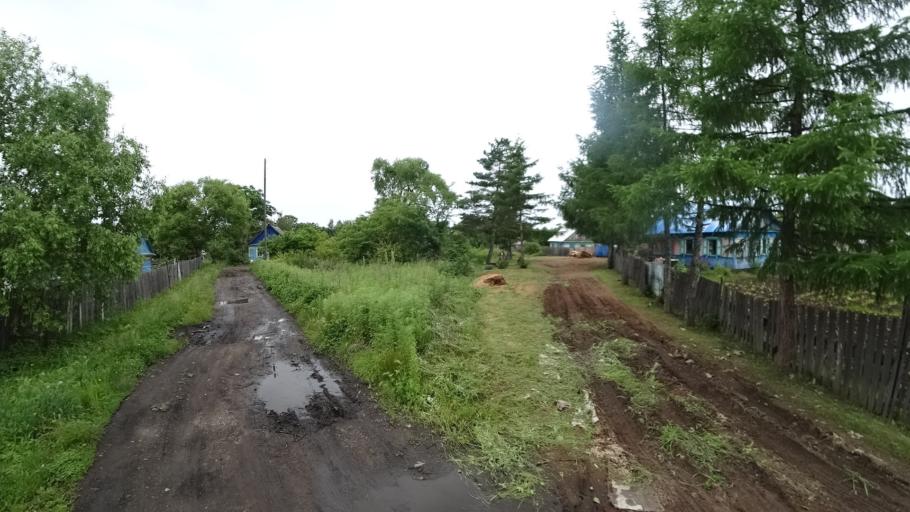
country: RU
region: Primorskiy
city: Novosysoyevka
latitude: 44.2087
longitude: 133.3258
